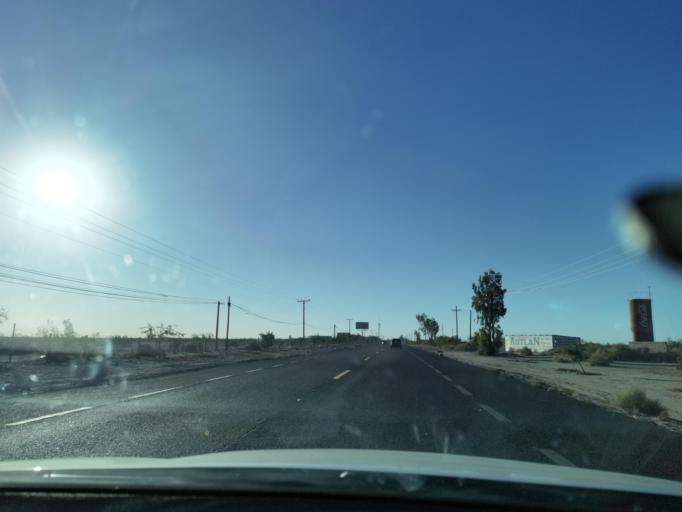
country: MX
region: Baja California
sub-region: Mexicali
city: Islas Agrarias Grupo A
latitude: 32.6323
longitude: -115.2662
